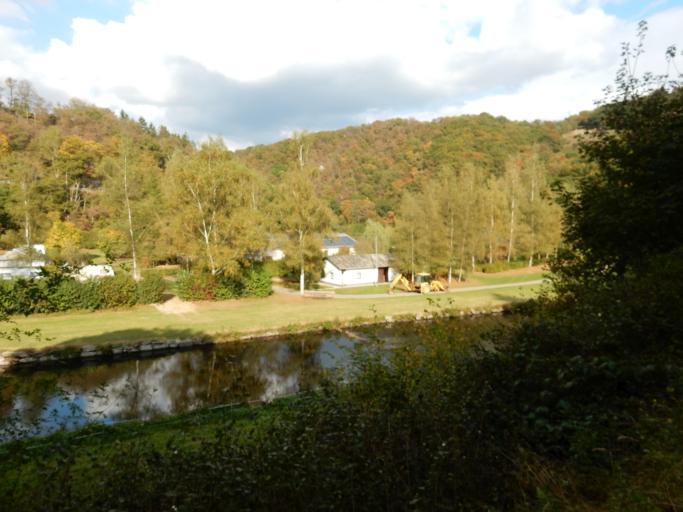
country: LU
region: Diekirch
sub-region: Canton de Wiltz
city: Goesdorf
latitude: 49.9128
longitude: 6.0004
